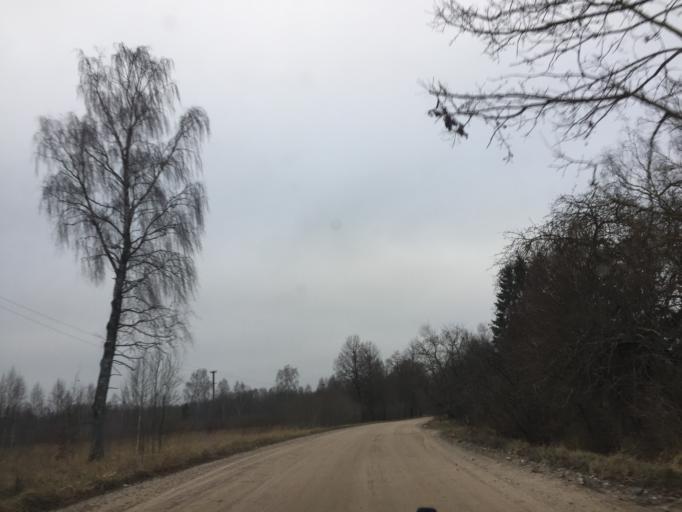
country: LV
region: Limbazu Rajons
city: Limbazi
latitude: 57.5717
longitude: 24.5210
